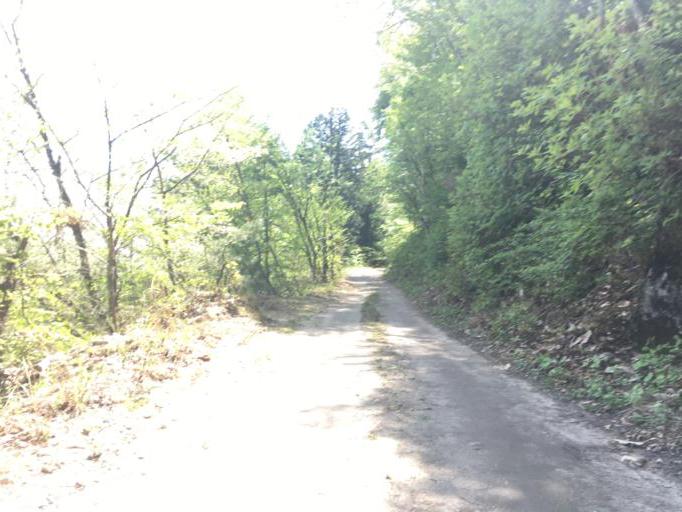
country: JP
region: Nagano
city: Omachi
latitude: 36.5129
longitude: 137.7938
